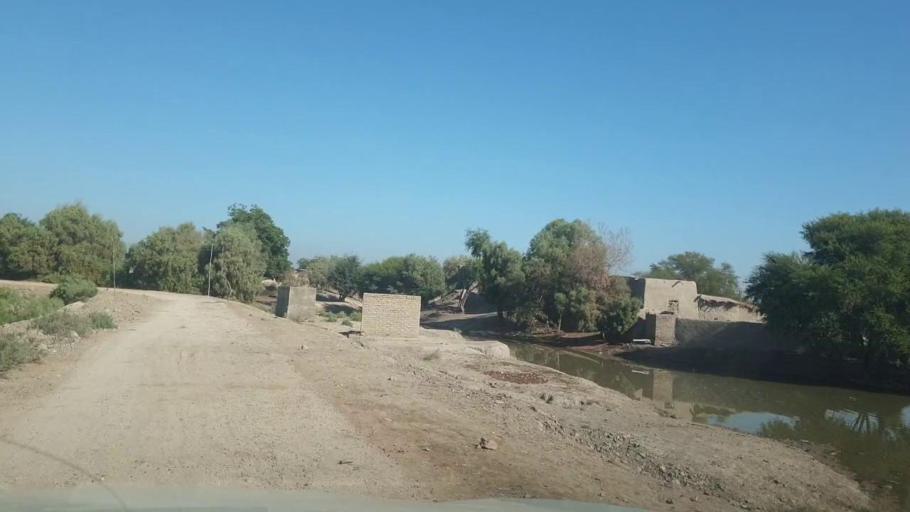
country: PK
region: Sindh
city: Bhan
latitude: 26.5493
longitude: 67.6543
